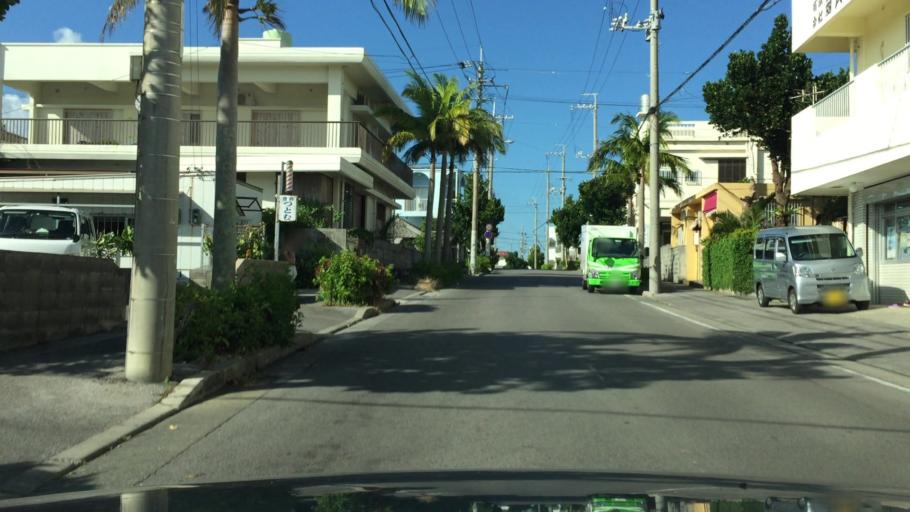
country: JP
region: Okinawa
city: Ishigaki
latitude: 24.3448
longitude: 124.1603
